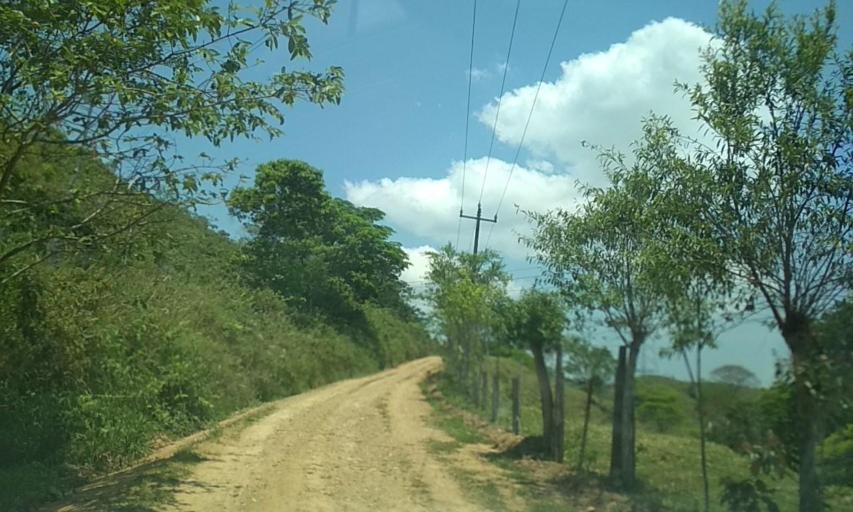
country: MX
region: Chiapas
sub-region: Tecpatan
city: Raudales Malpaso
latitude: 17.3963
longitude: -93.7455
